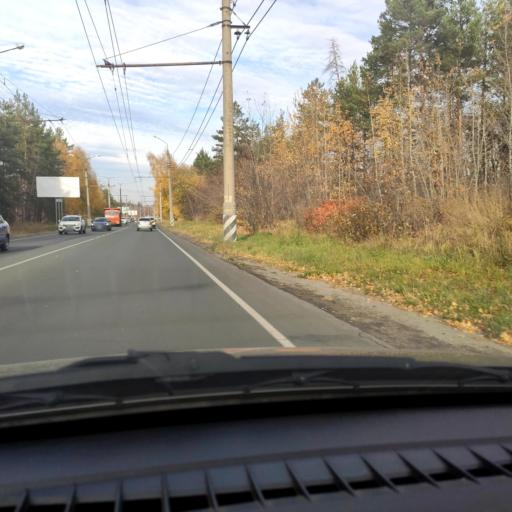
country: RU
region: Samara
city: Tol'yatti
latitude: 53.4915
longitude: 49.3855
